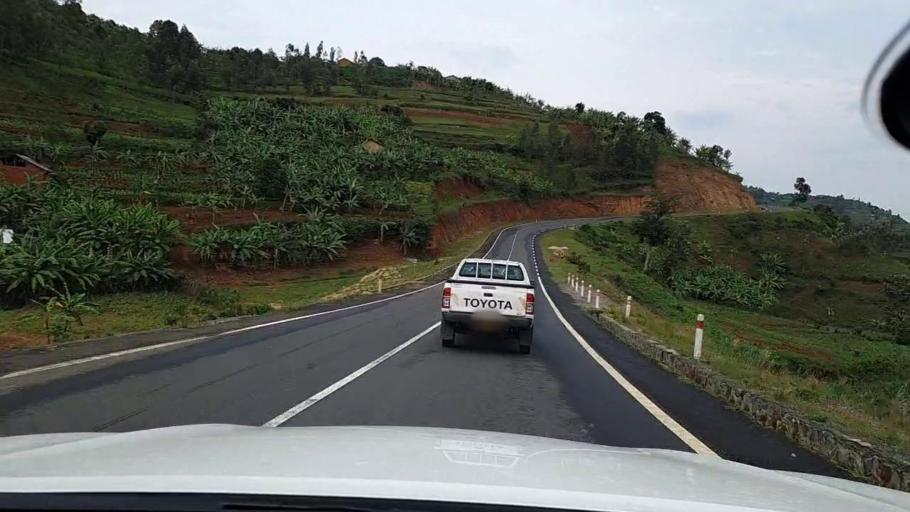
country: RW
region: Western Province
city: Kibuye
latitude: -2.1664
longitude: 29.2965
